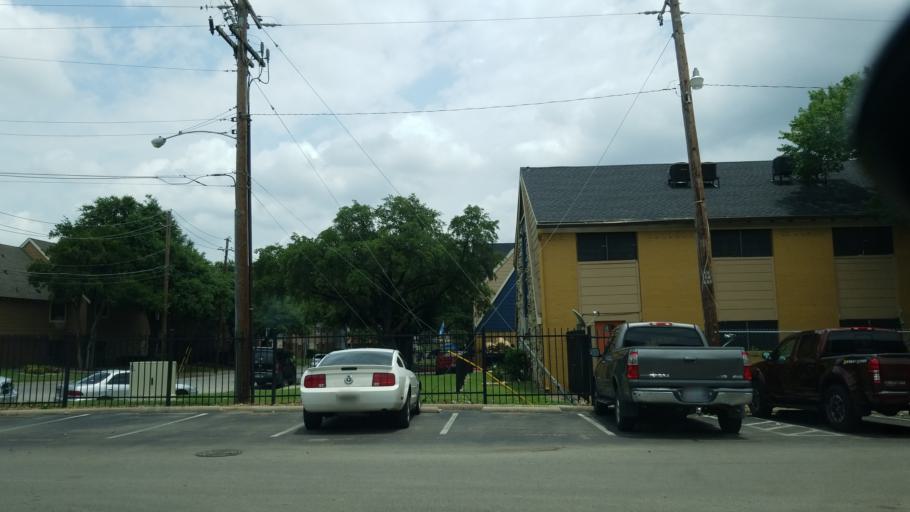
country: US
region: Texas
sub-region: Dallas County
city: Farmers Branch
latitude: 32.8715
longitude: -96.8682
